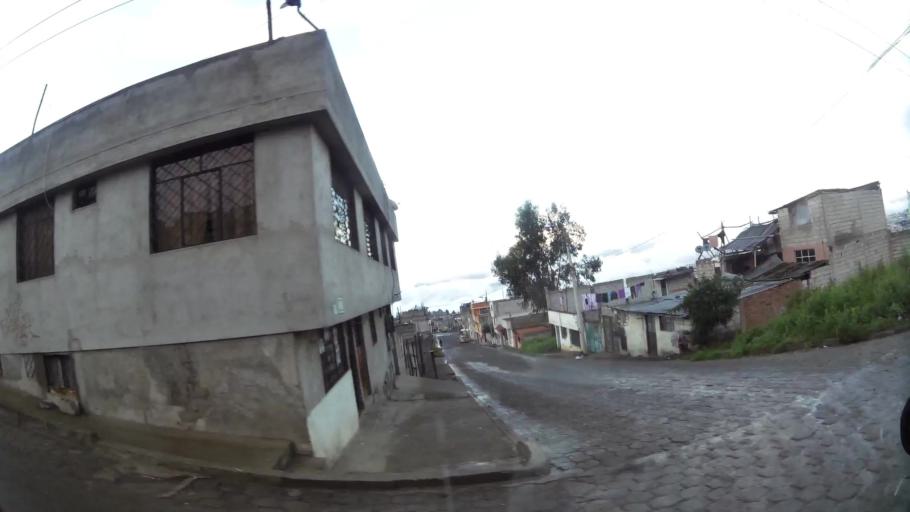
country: EC
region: Pichincha
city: Quito
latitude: -0.0974
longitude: -78.5153
